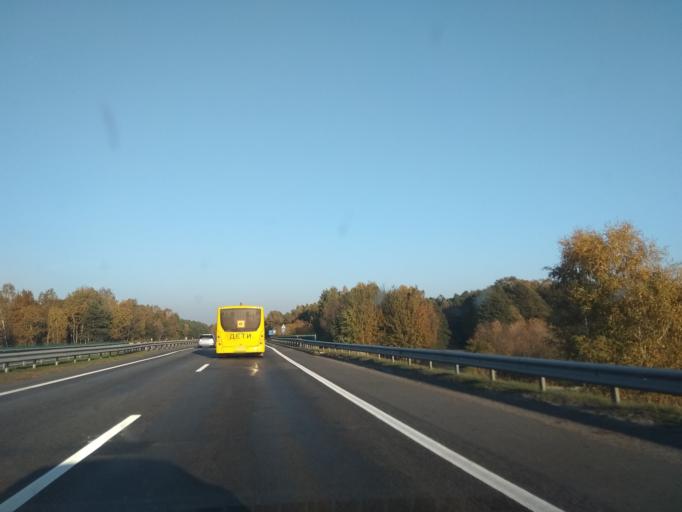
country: BY
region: Brest
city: Zhabinka
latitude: 52.1741
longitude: 24.1491
